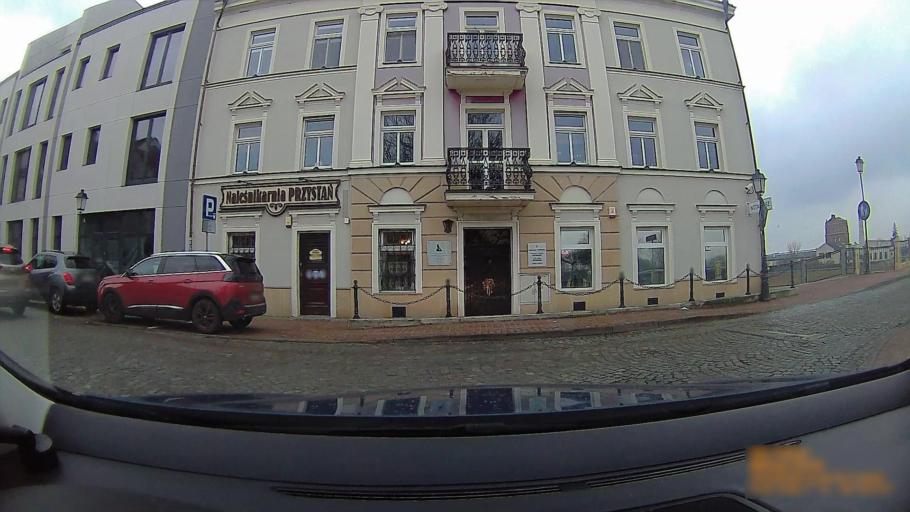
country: PL
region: Greater Poland Voivodeship
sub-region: Konin
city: Konin
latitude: 52.2126
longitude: 18.2552
